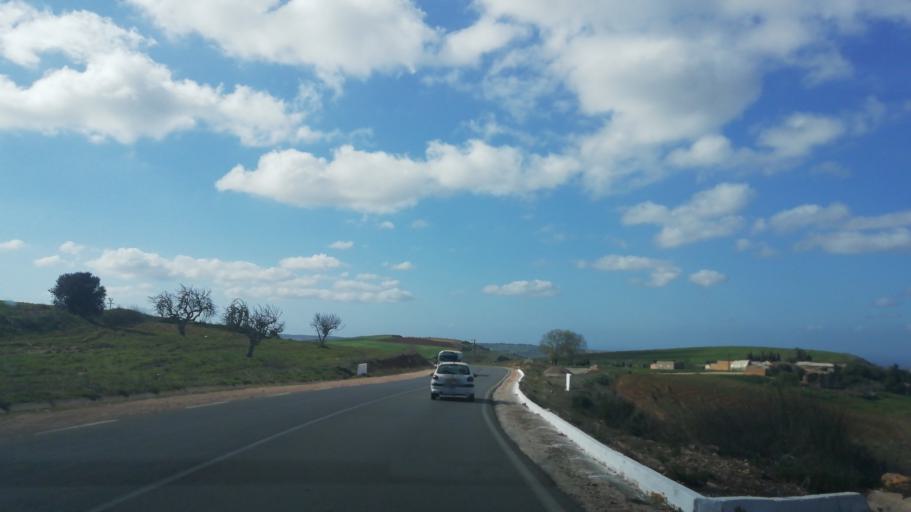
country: DZ
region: Relizane
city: Relizane
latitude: 36.0928
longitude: 0.4608
